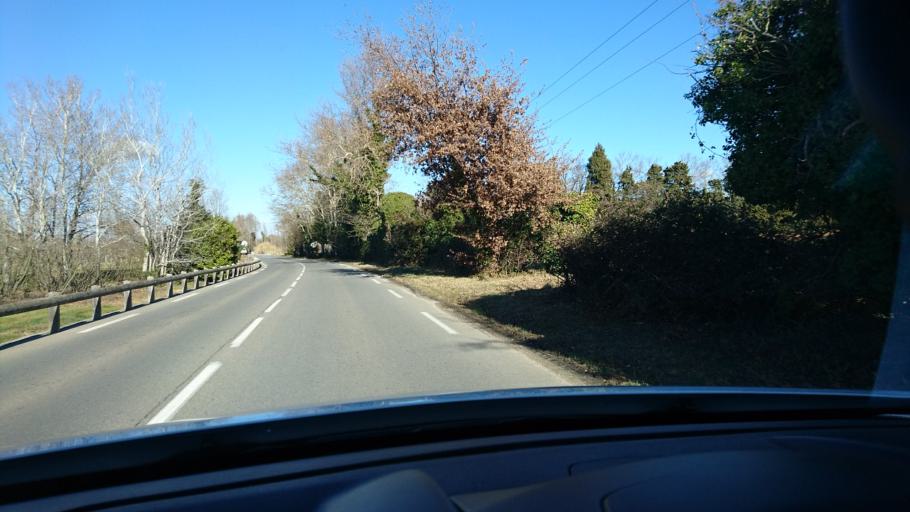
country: FR
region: Provence-Alpes-Cote d'Azur
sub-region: Departement du Vaucluse
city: Morieres-les-Avignon
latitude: 43.9134
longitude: 4.9071
